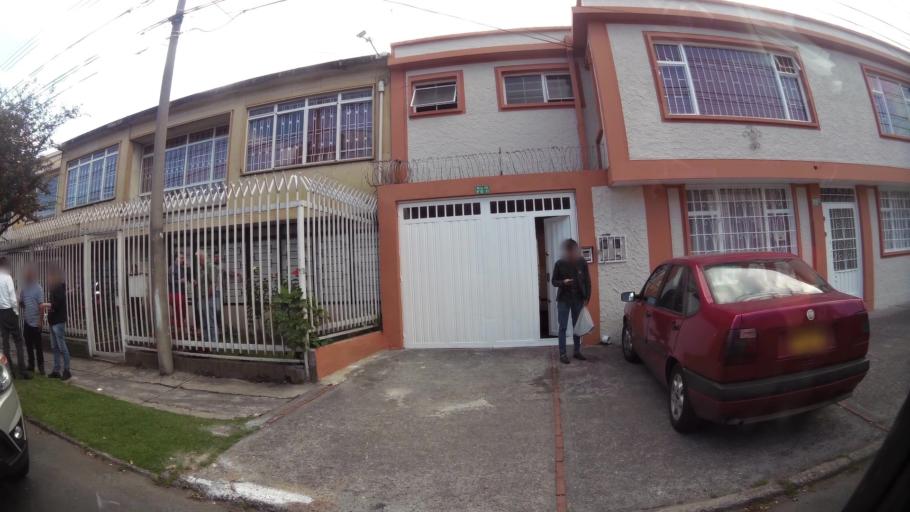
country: CO
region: Bogota D.C.
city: Bogota
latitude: 4.6503
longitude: -74.0701
